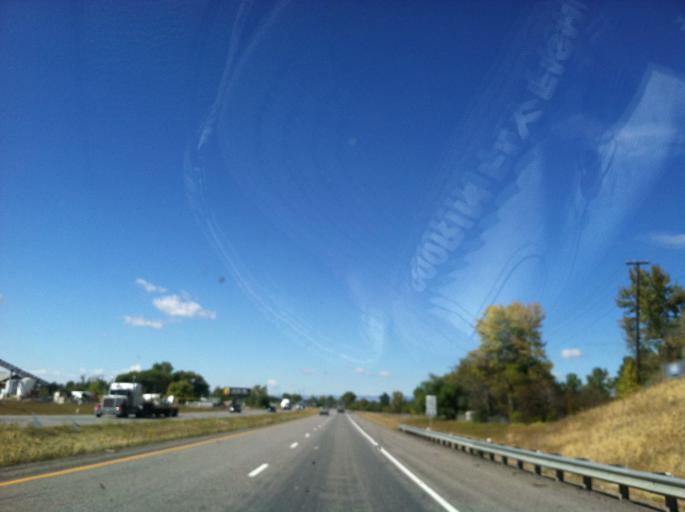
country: US
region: Montana
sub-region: Gallatin County
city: Bozeman
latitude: 45.6849
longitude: -111.0150
